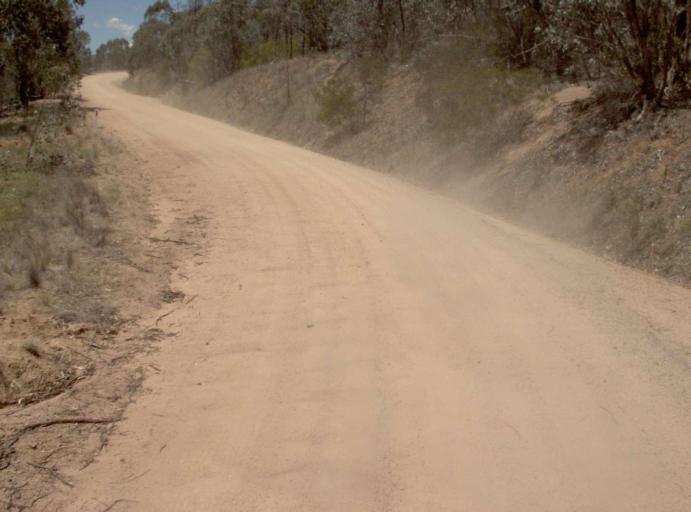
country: AU
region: New South Wales
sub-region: Snowy River
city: Jindabyne
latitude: -36.9204
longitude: 148.3916
